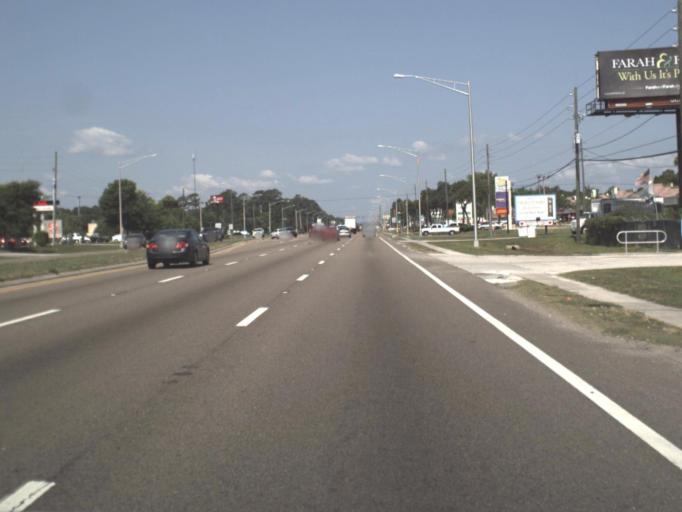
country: US
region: Florida
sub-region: Duval County
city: Jacksonville
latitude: 30.2869
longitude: -81.5341
